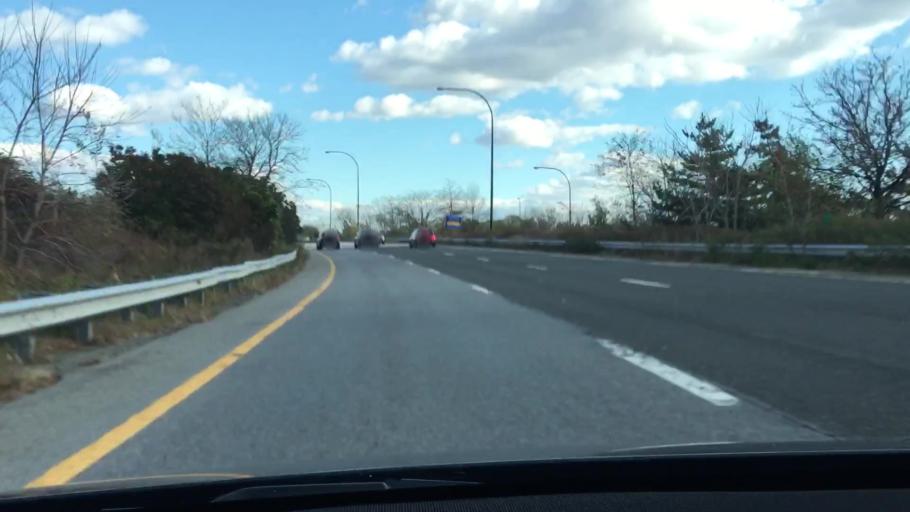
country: US
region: New York
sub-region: Nassau County
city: Carle Place
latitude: 40.7556
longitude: -73.6184
